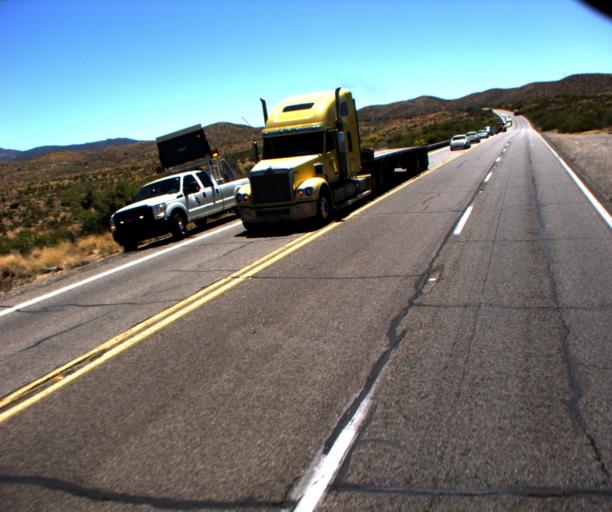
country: US
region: Arizona
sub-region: Pinal County
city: Oracle
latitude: 32.6518
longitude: -110.7055
